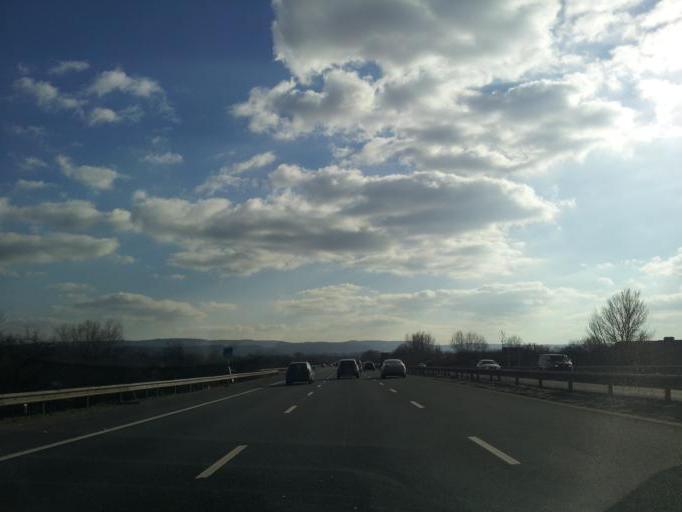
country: GB
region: England
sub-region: Somerset
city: Creech Saint Michael
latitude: 51.0168
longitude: -3.0642
